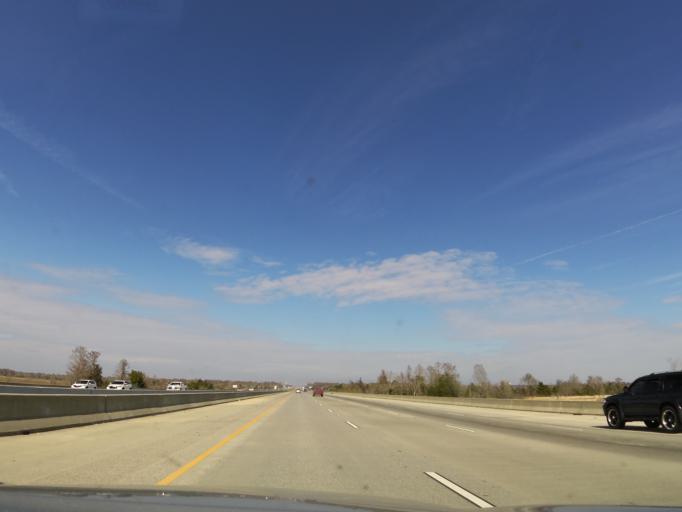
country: US
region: Georgia
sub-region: McIntosh County
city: Darien
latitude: 31.3535
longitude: -81.4604
